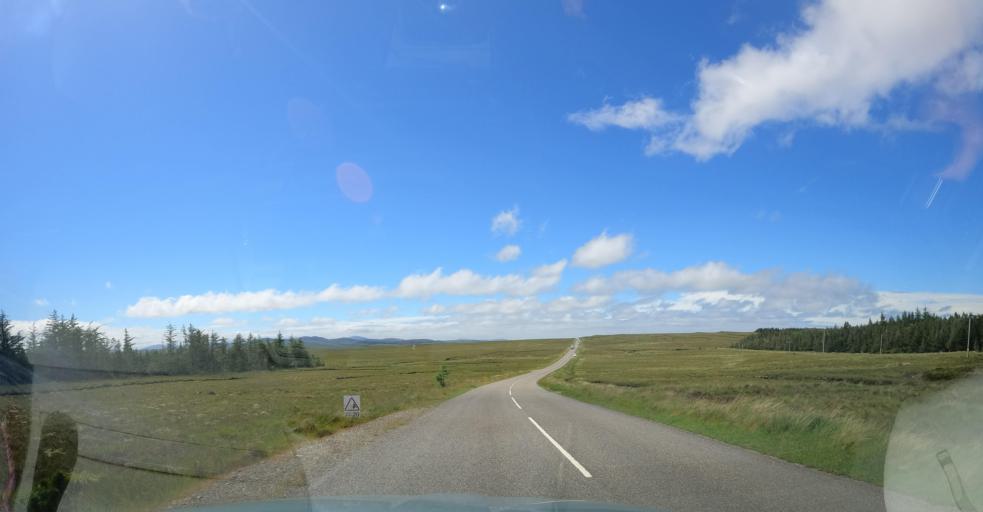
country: GB
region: Scotland
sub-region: Eilean Siar
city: Isle of Lewis
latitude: 58.1808
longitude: -6.6601
